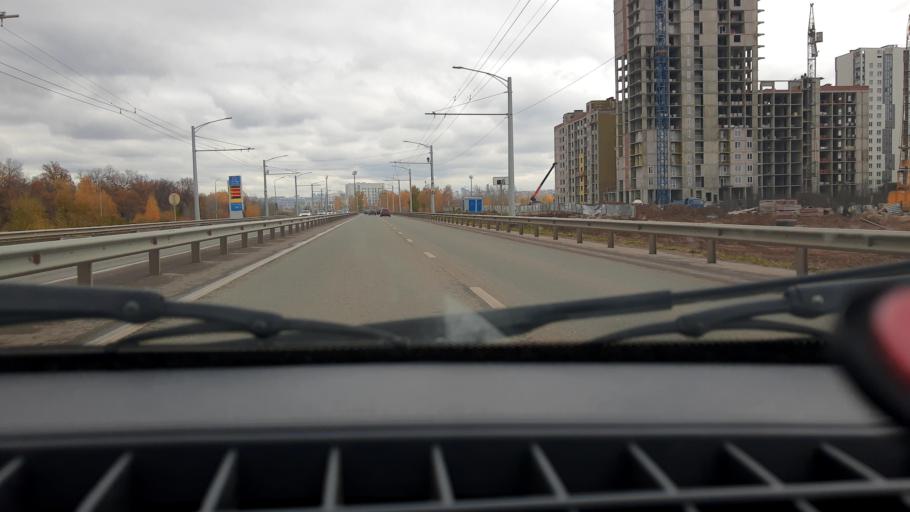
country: RU
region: Bashkortostan
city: Mikhaylovka
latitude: 54.7726
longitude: 55.9007
